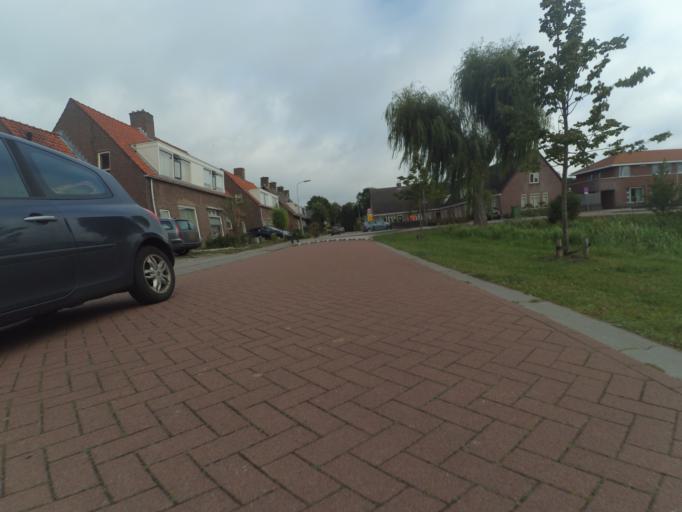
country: NL
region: Utrecht
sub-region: Gemeente Utrechtse Heuvelrug
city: Overberg
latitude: 52.0818
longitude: 5.4867
